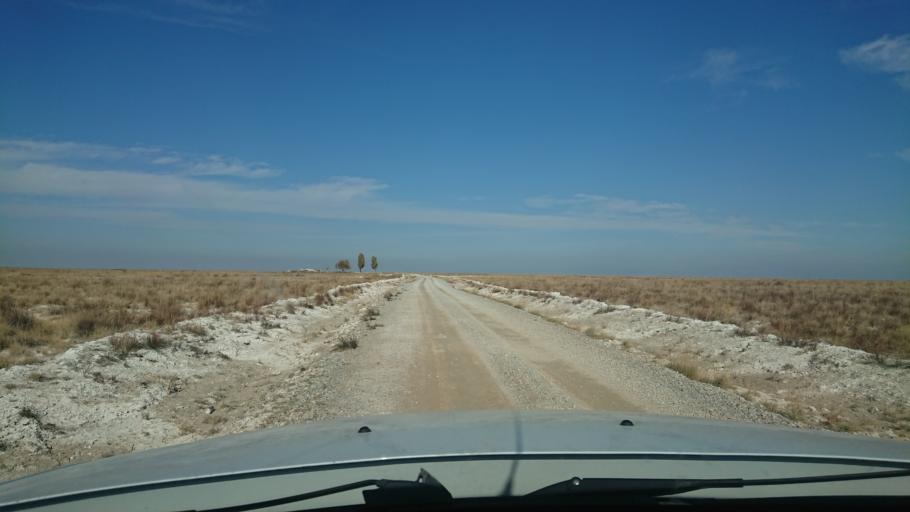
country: TR
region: Aksaray
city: Eskil
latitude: 38.4708
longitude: 33.4567
